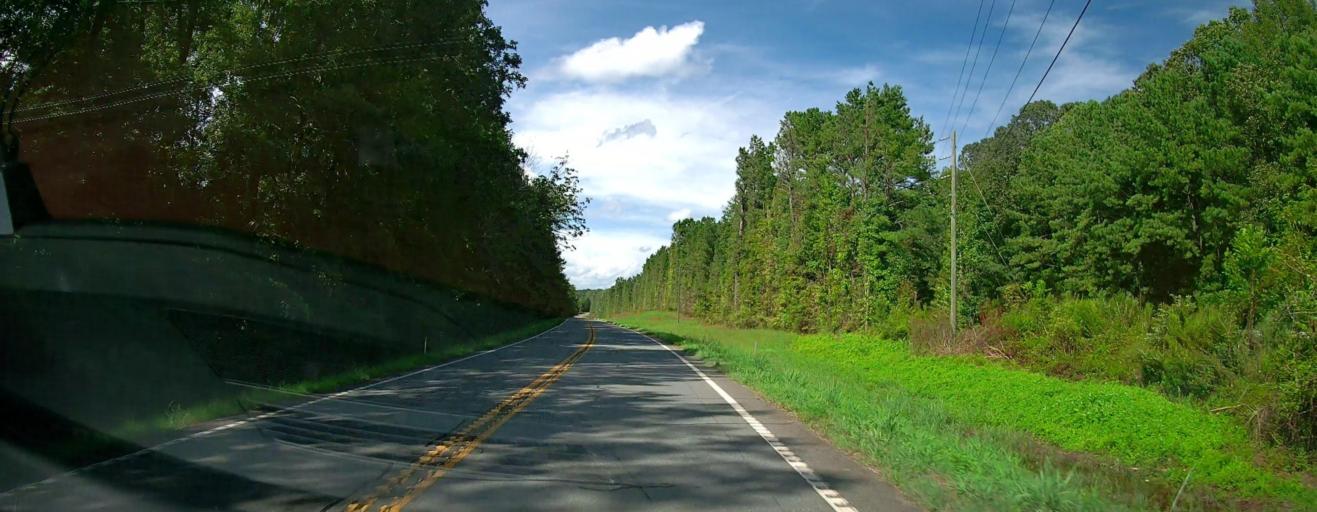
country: US
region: Georgia
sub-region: Talbot County
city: Talbotton
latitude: 32.7356
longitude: -84.5542
